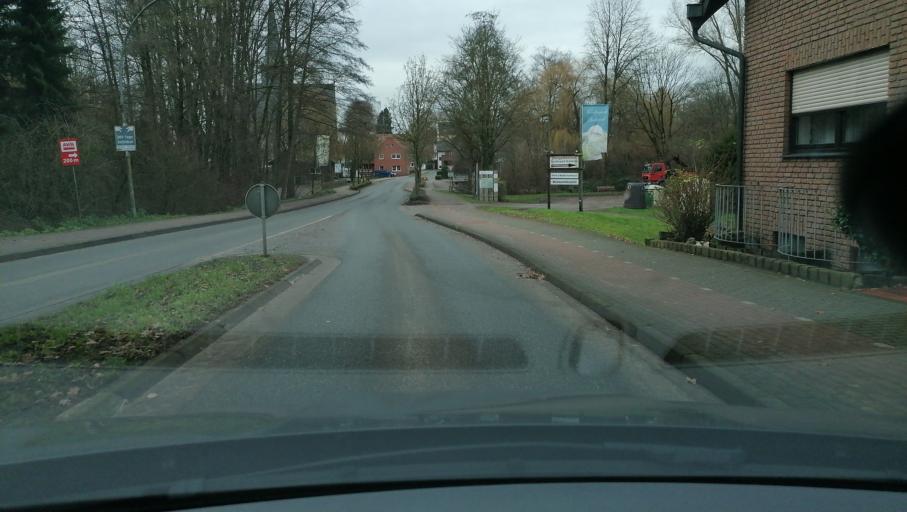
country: DE
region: North Rhine-Westphalia
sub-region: Regierungsbezirk Munster
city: Klein Reken
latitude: 51.7865
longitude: 7.0413
